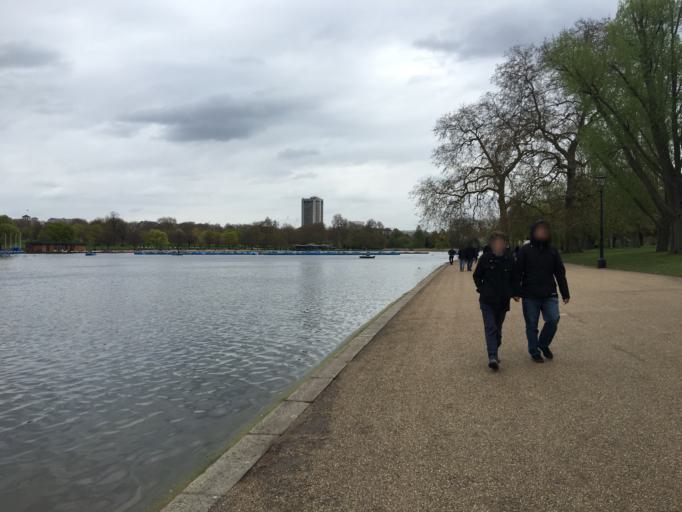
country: GB
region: England
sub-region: Greater London
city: Chelsea
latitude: 51.5046
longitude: -0.1666
